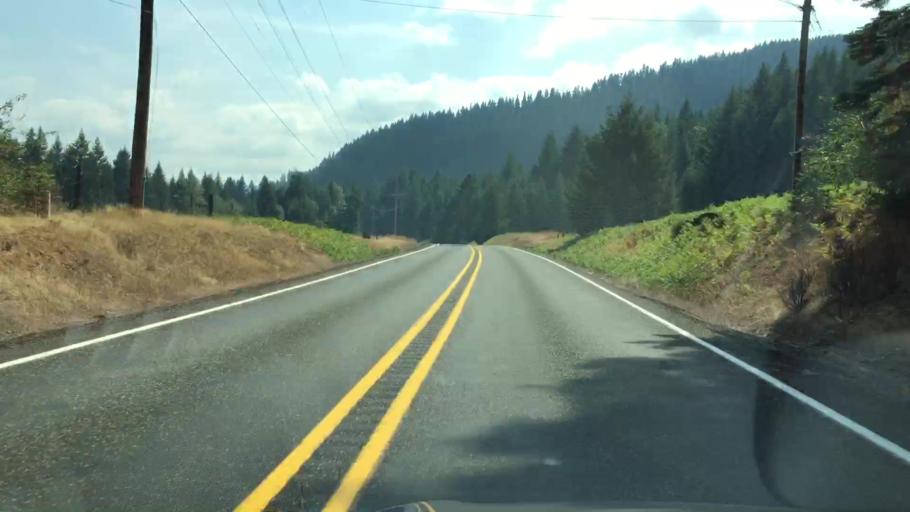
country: US
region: Washington
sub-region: Klickitat County
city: White Salmon
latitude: 45.8830
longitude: -121.5213
